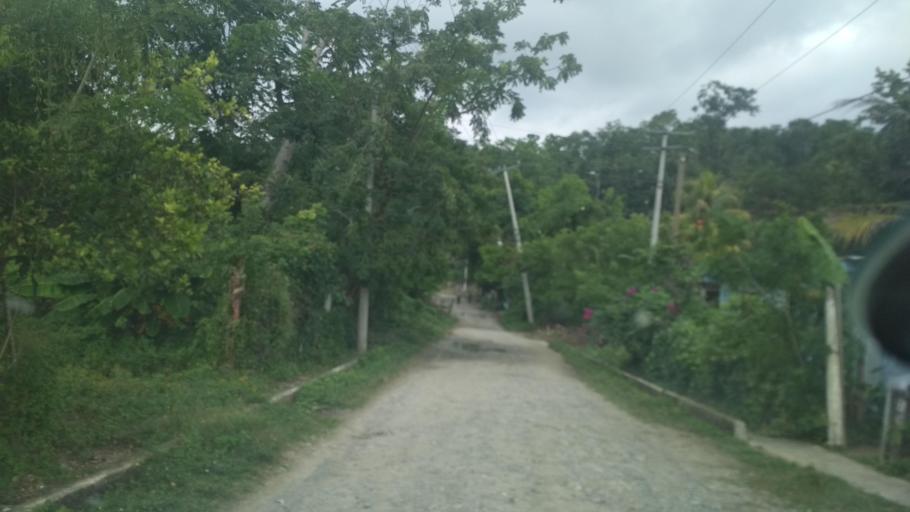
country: MX
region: Veracruz
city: Papantla de Olarte
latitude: 20.4803
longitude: -97.3556
